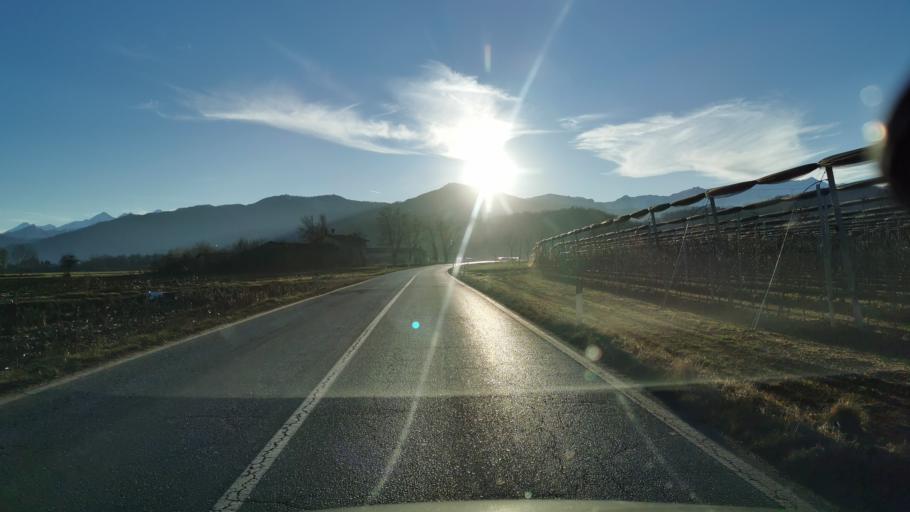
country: IT
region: Piedmont
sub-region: Provincia di Cuneo
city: Caraglio
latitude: 44.4308
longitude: 7.4396
